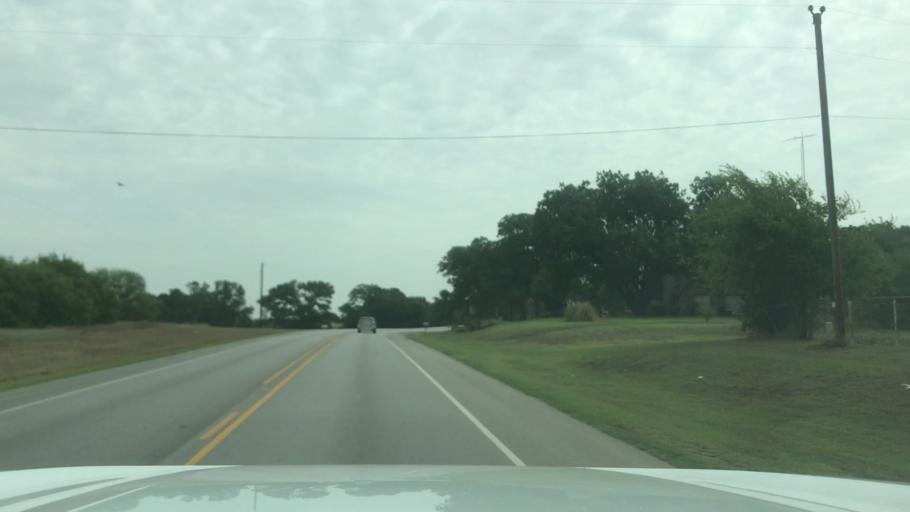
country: US
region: Texas
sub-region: Erath County
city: Dublin
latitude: 32.0982
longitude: -98.3996
